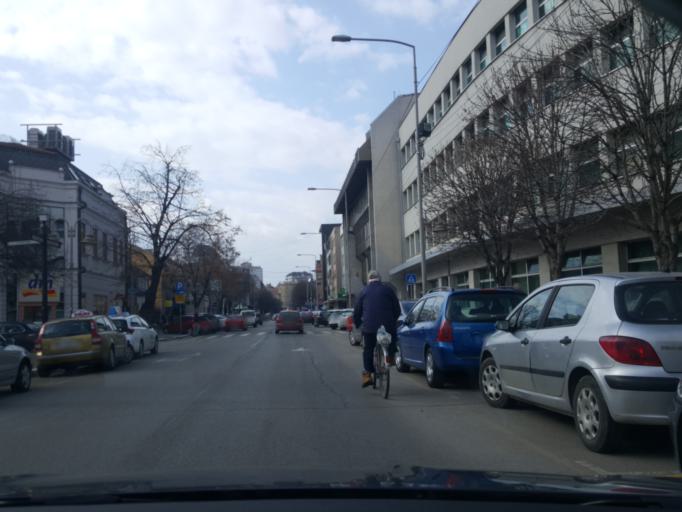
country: RS
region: Central Serbia
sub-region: Nisavski Okrug
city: Nis
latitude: 43.3180
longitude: 21.8970
